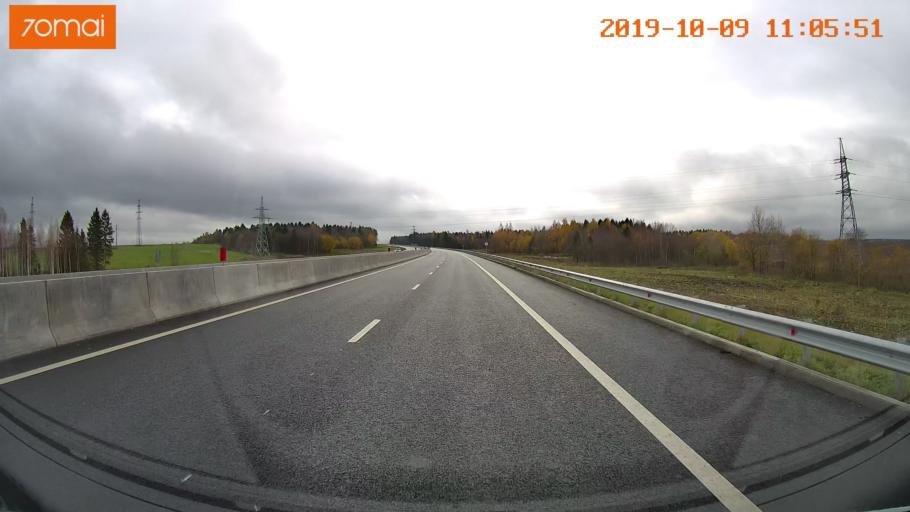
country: RU
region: Vologda
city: Molochnoye
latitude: 59.1941
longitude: 39.7581
